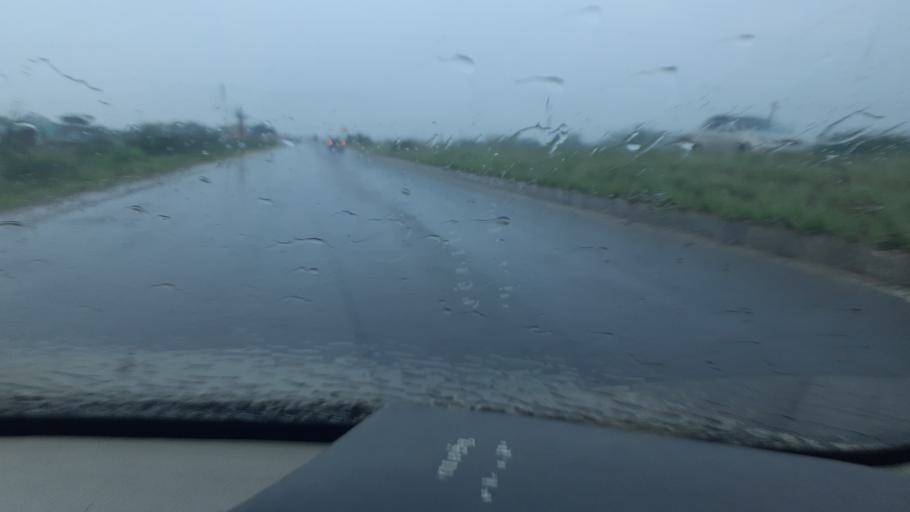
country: IN
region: Tamil Nadu
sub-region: Virudhunagar
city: Sattur
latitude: 9.4198
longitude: 77.9168
